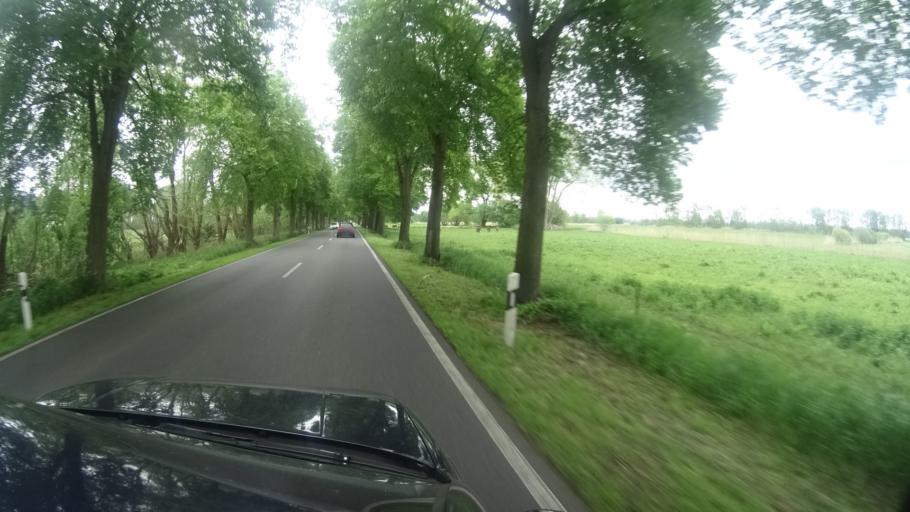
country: DE
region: Brandenburg
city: Fehrbellin
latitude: 52.8286
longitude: 12.7750
